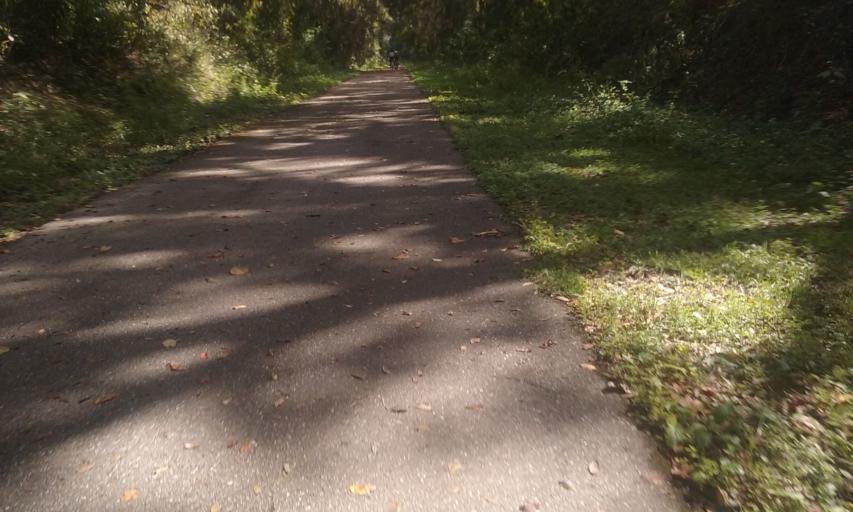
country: US
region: Florida
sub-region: Alachua County
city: Hawthorne
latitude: 29.5949
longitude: -82.1373
